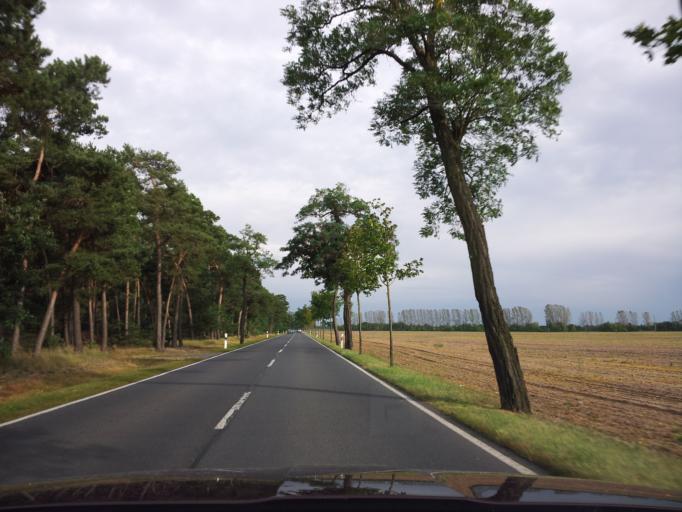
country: DE
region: Brandenburg
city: Beelitz
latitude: 52.1334
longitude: 12.9990
